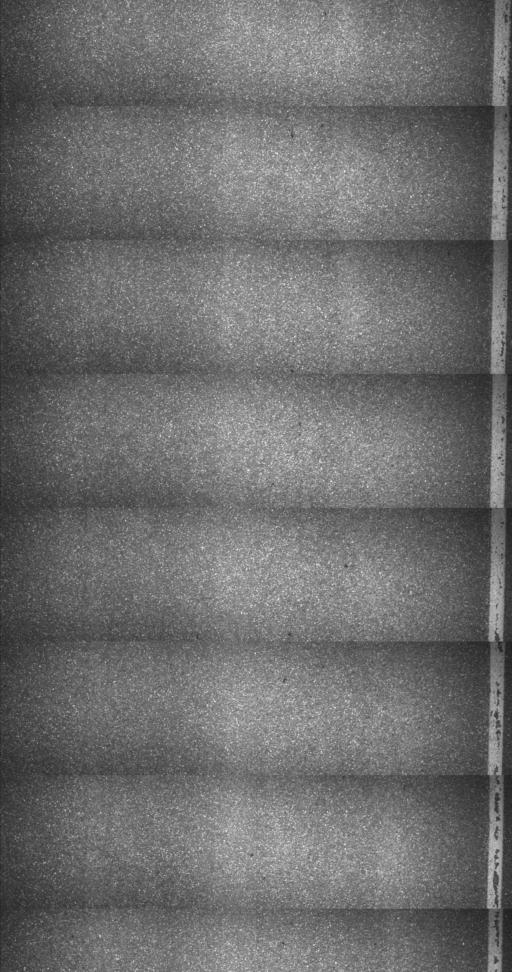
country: US
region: Vermont
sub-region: Washington County
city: Northfield
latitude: 44.1145
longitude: -72.6231
